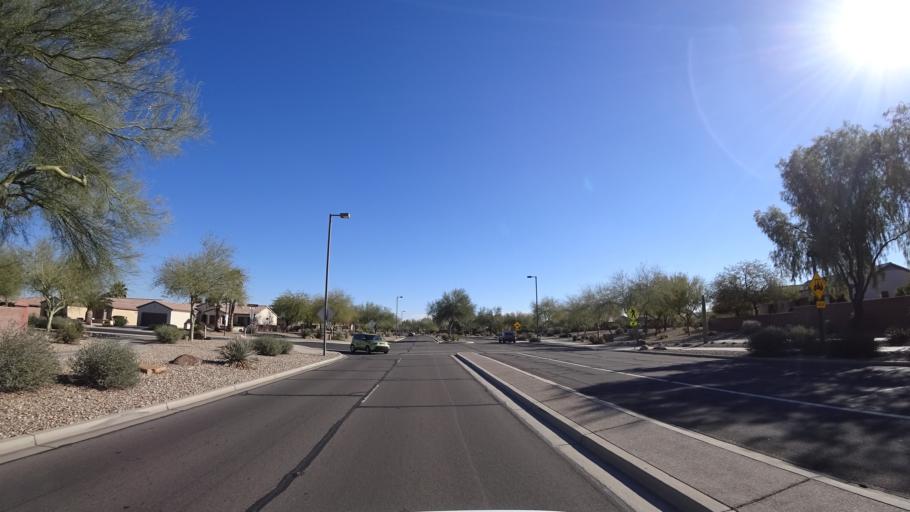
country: US
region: Arizona
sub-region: Maricopa County
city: Sun City West
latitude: 33.6648
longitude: -112.3917
